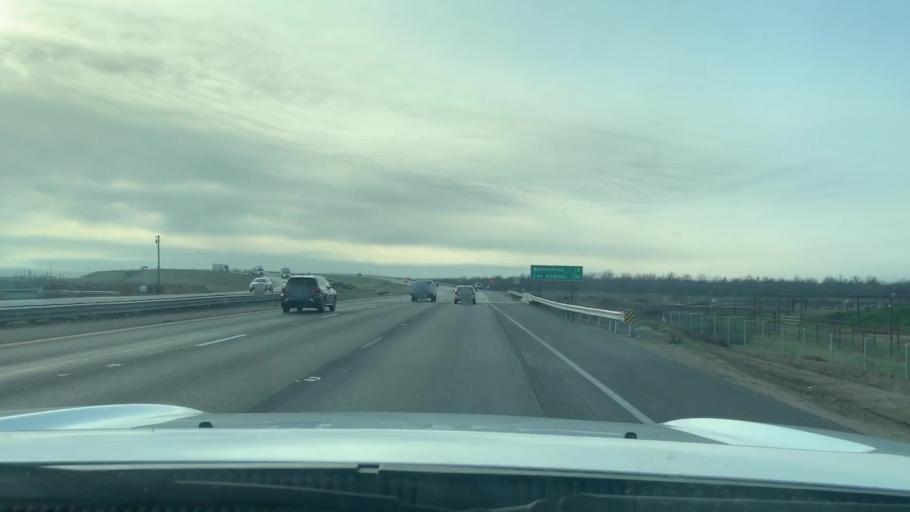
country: US
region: California
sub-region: Kern County
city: McFarland
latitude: 35.5974
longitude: -119.2103
